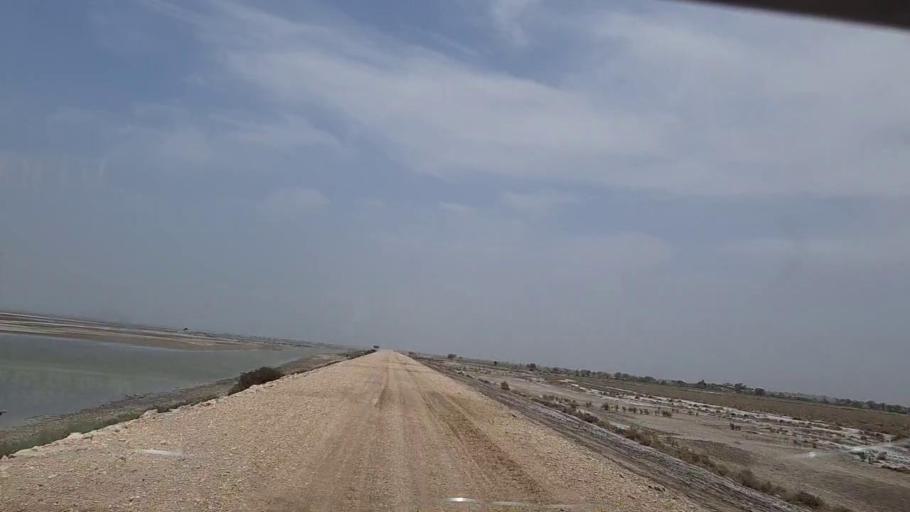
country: PK
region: Sindh
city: Sehwan
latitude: 26.4151
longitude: 67.7620
